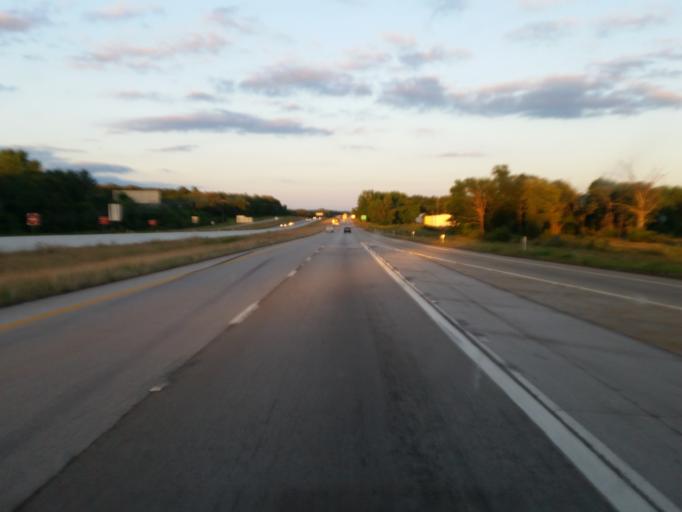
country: US
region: Texas
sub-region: Van Zandt County
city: Van
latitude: 32.4982
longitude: -95.5825
